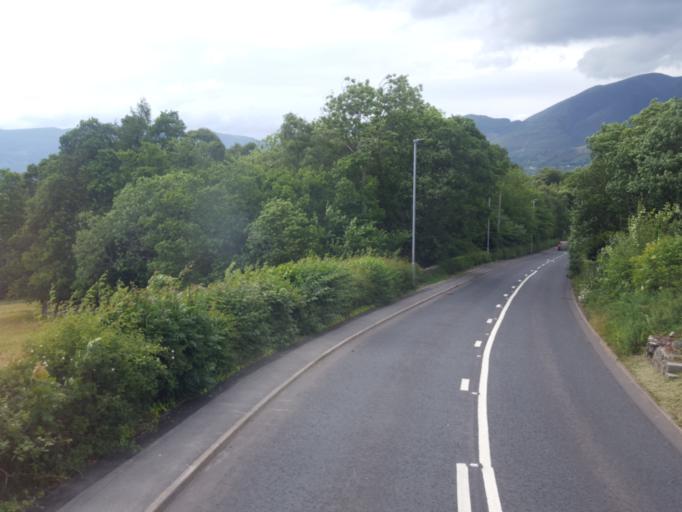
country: GB
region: England
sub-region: Cumbria
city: Keswick
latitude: 54.5967
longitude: -3.1162
